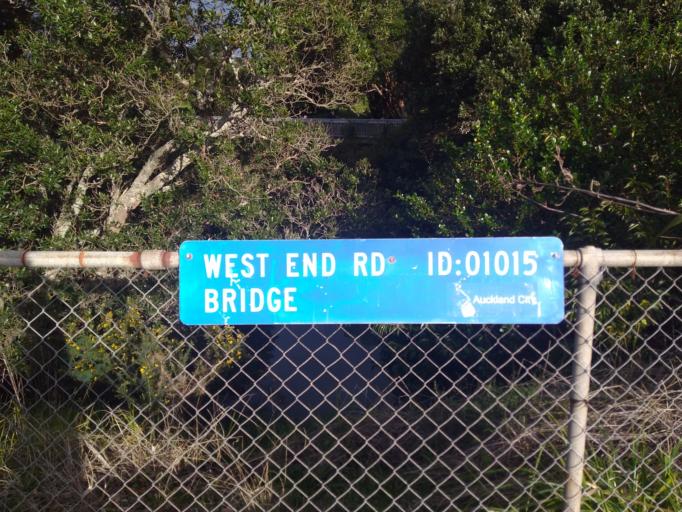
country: NZ
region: Auckland
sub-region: Auckland
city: Auckland
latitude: -36.8507
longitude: 174.7254
